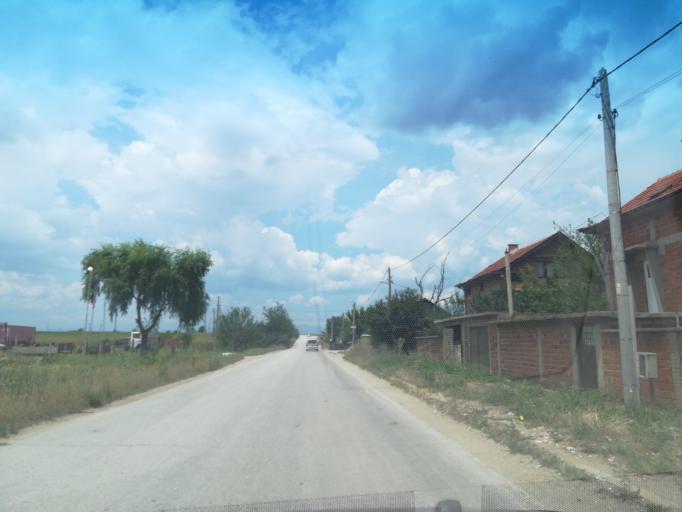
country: BG
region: Stara Zagora
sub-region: Obshtina Chirpan
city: Chirpan
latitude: 42.1781
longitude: 25.2072
